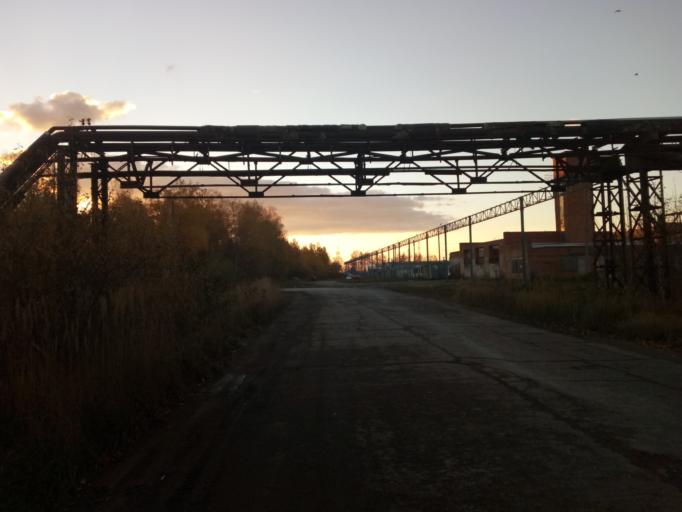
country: RU
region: Tatarstan
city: Staroye Arakchino
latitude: 55.8820
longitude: 48.9693
